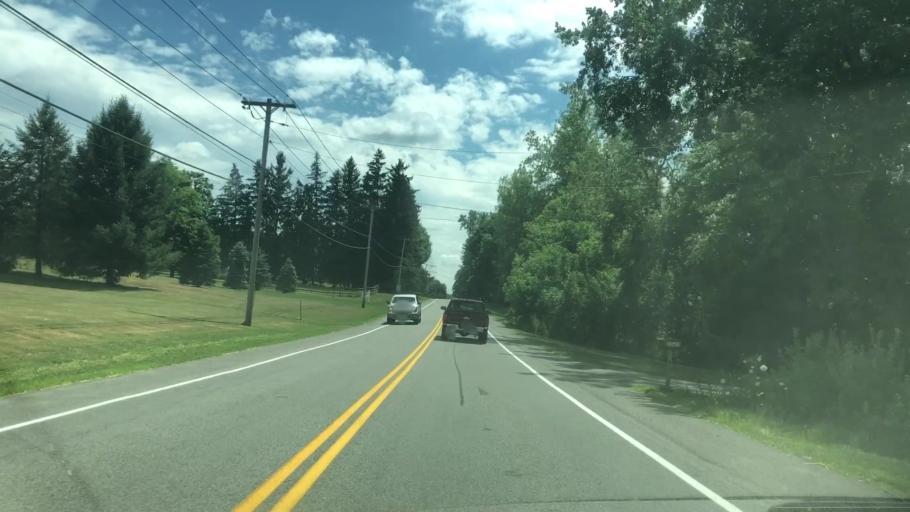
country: US
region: New York
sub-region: Monroe County
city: Fairport
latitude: 43.1351
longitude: -77.4006
